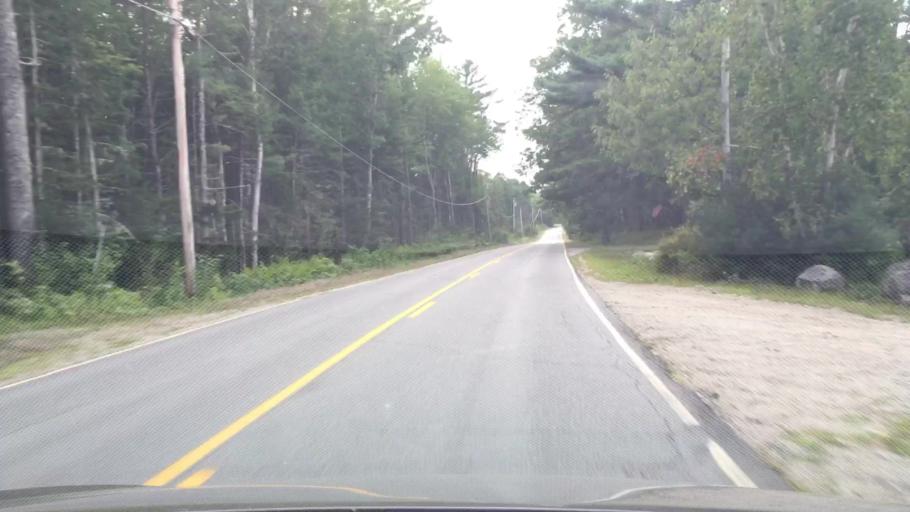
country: US
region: Maine
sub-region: Hancock County
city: Penobscot
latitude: 44.4505
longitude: -68.6948
